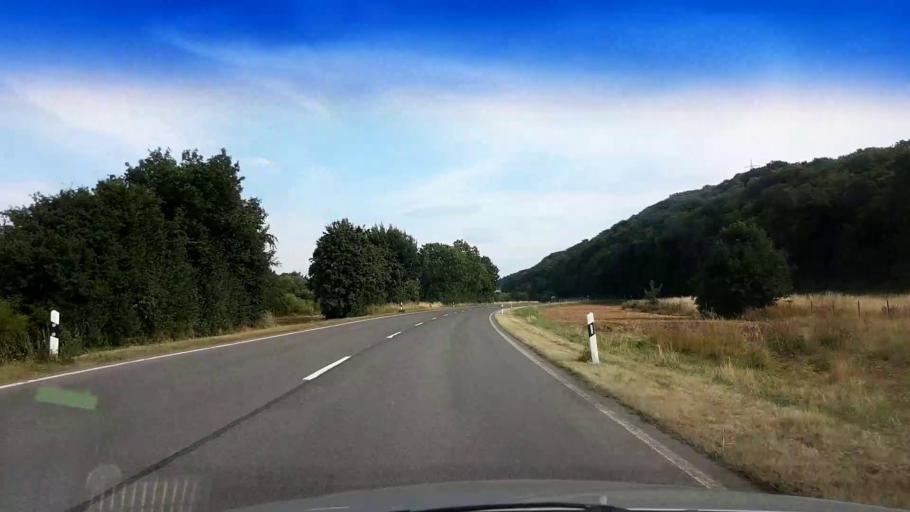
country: DE
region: Bavaria
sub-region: Regierungsbezirk Unterfranken
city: Stettfeld
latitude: 49.9582
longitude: 10.7144
